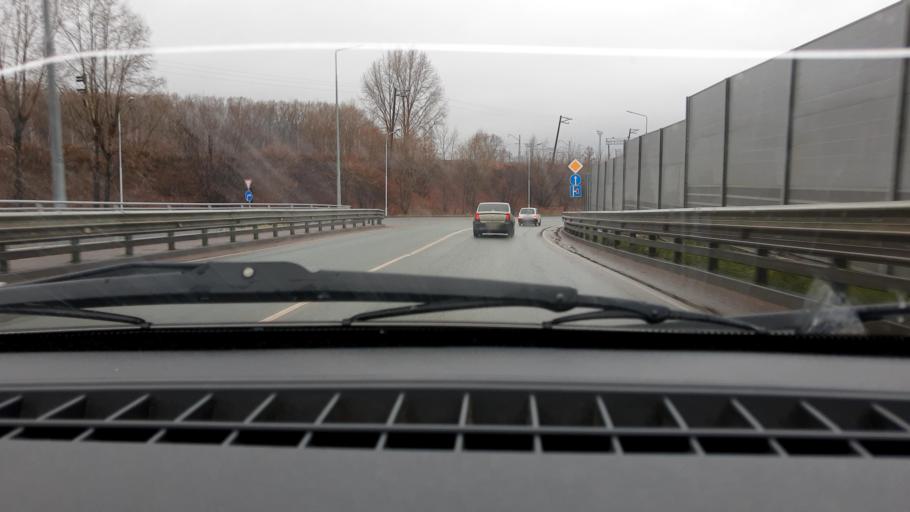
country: RU
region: Bashkortostan
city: Ufa
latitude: 54.8289
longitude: 56.1299
